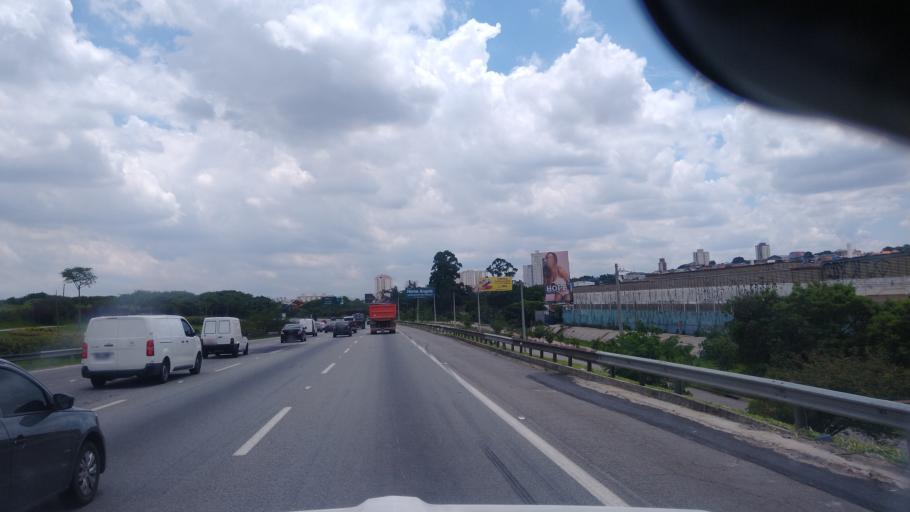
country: BR
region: Sao Paulo
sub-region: Guarulhos
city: Guarulhos
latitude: -23.4933
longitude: -46.5407
